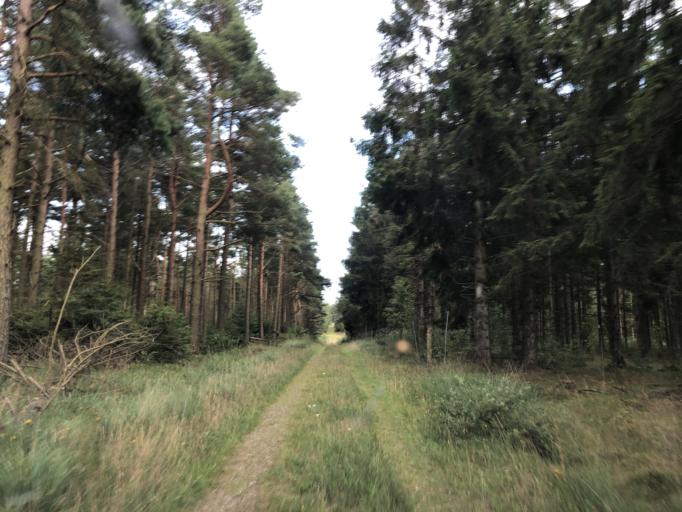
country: DK
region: Central Jutland
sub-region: Holstebro Kommune
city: Ulfborg
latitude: 56.2859
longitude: 8.4170
